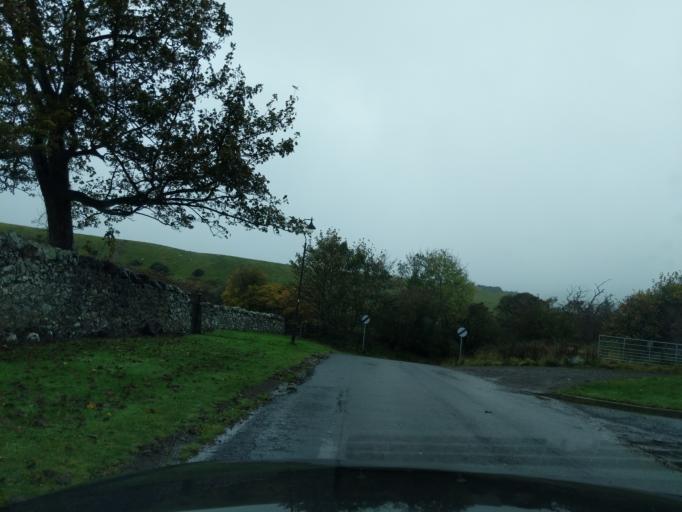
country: GB
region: Scotland
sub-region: East Lothian
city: Dunbar
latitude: 55.9285
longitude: -2.4208
